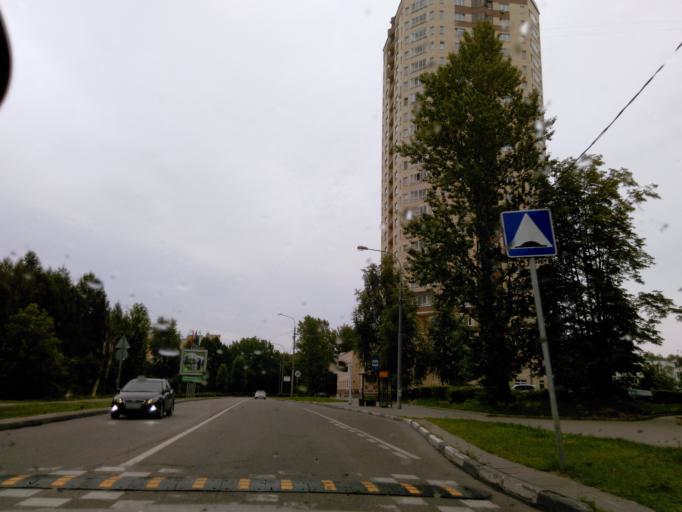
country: RU
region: Moskovskaya
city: Rzhavki
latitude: 55.9997
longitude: 37.2184
